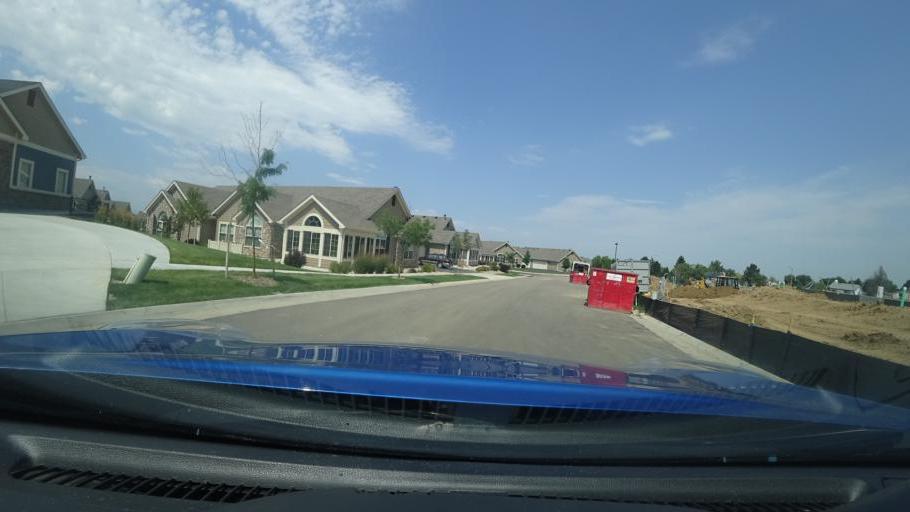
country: US
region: Colorado
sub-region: Adams County
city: Aurora
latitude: 39.6811
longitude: -104.7596
